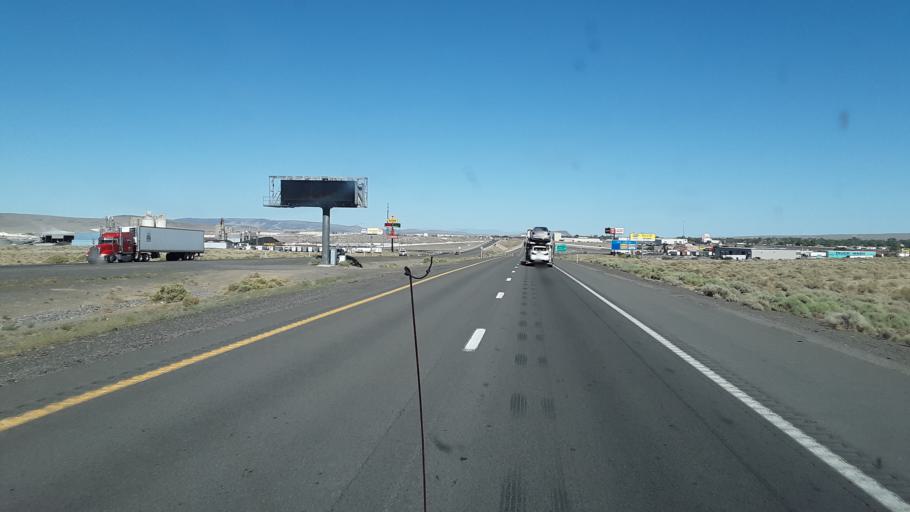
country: US
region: Nevada
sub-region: Lyon County
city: Fernley
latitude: 39.6169
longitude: -119.2745
